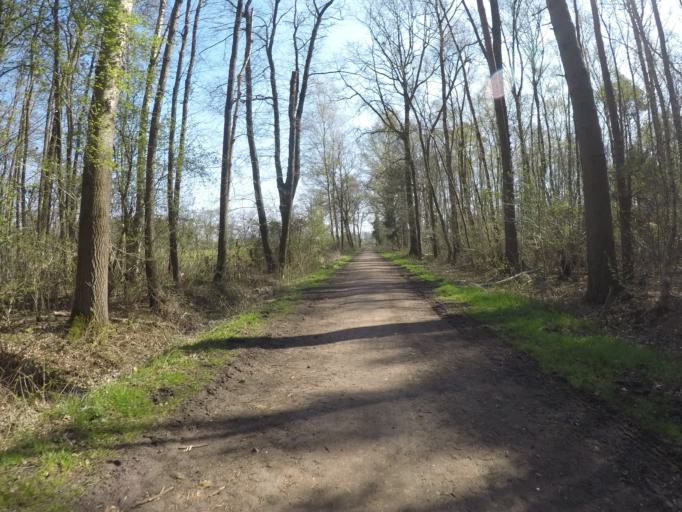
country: DE
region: Schleswig-Holstein
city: Rellingen
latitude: 53.6136
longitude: 9.7813
